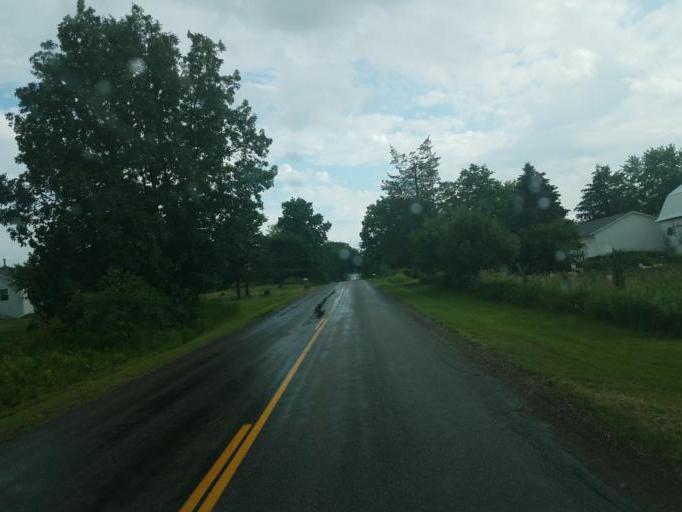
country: US
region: Michigan
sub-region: Eaton County
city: Bellevue
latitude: 42.5254
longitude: -85.0137
